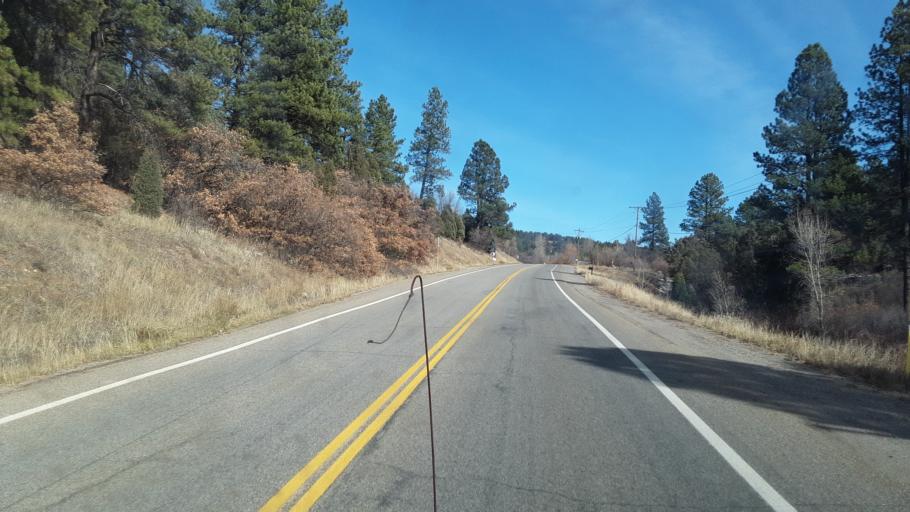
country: US
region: Colorado
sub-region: La Plata County
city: Durango
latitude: 37.3073
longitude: -107.8181
